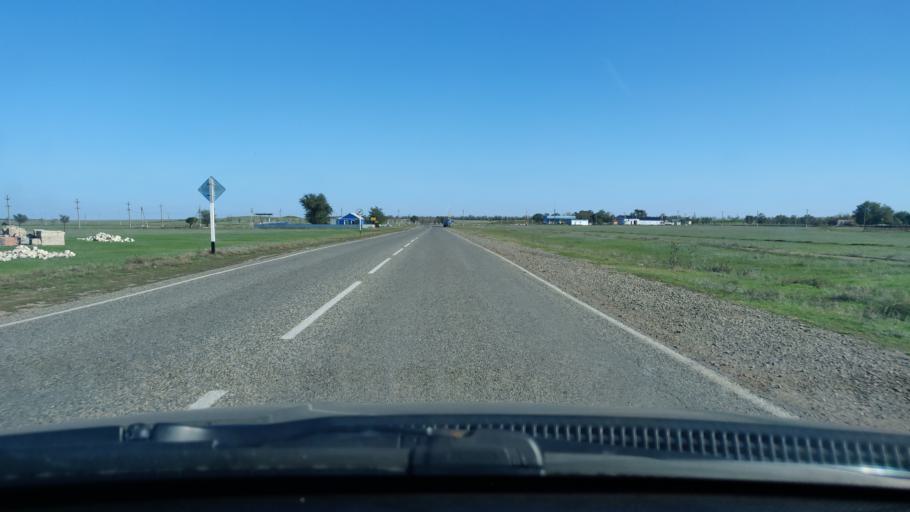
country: RU
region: Stavropol'skiy
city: Letnyaya Stavka
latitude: 45.3743
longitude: 43.6870
